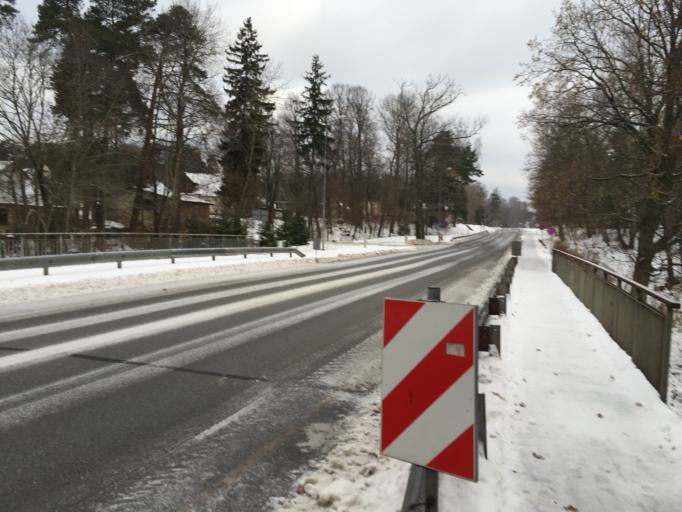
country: LV
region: Saulkrastu
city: Saulkrasti
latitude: 57.2778
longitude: 24.4172
